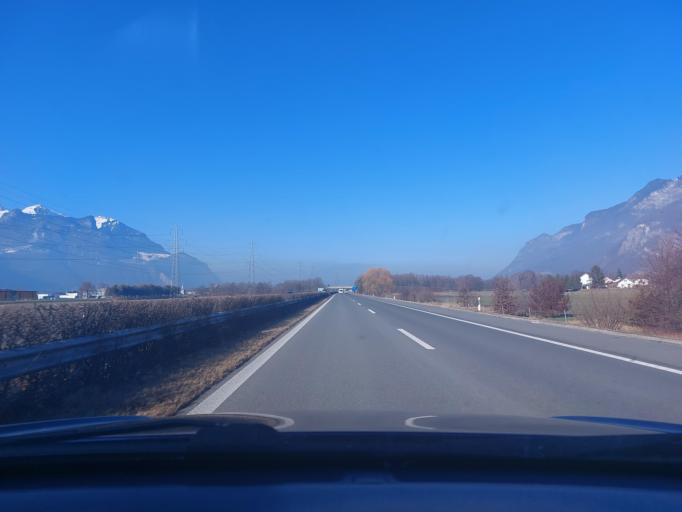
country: CH
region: Vaud
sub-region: Aigle District
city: Aigle
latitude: 46.3099
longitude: 6.9489
